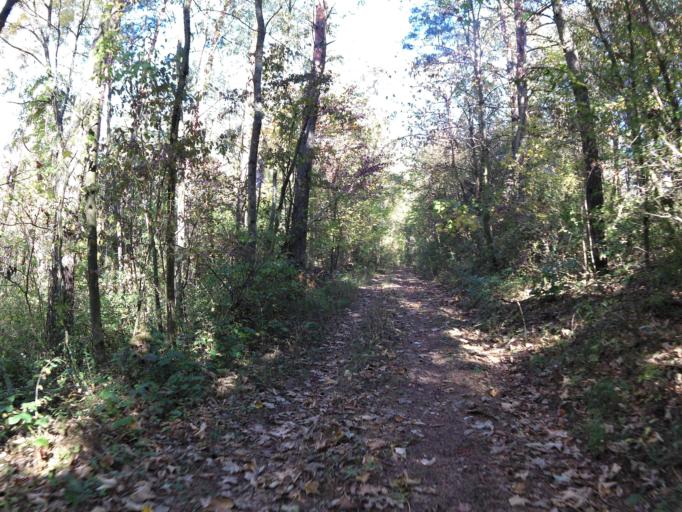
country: DE
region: Bavaria
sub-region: Regierungsbezirk Unterfranken
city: Eibelstadt
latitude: 49.7176
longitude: 9.9851
